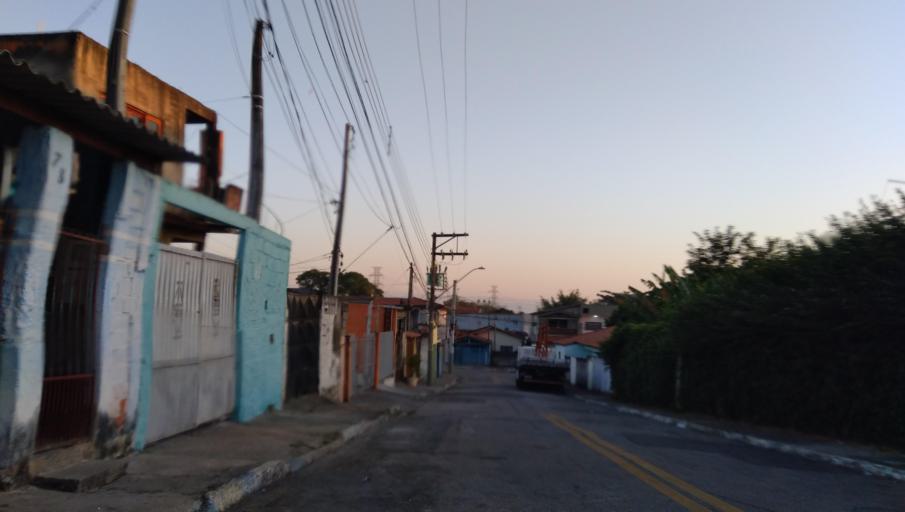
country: BR
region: Sao Paulo
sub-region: Sao Jose Dos Campos
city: Sao Jose dos Campos
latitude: -23.1720
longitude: -45.8179
